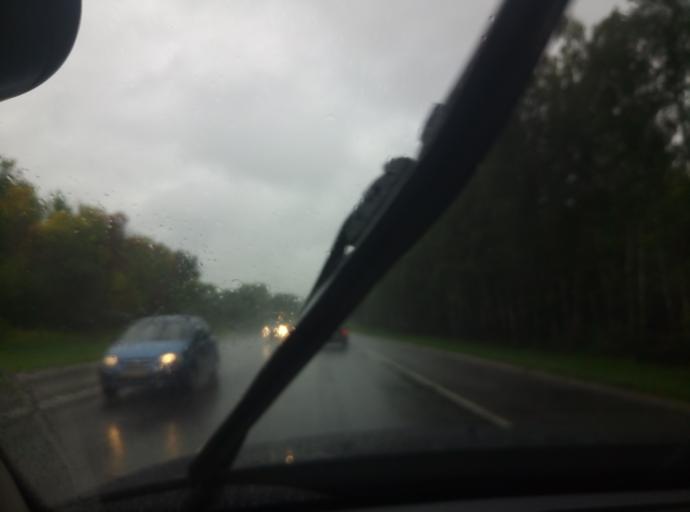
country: RU
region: Tula
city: Leninskiy
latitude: 54.3626
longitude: 37.5296
